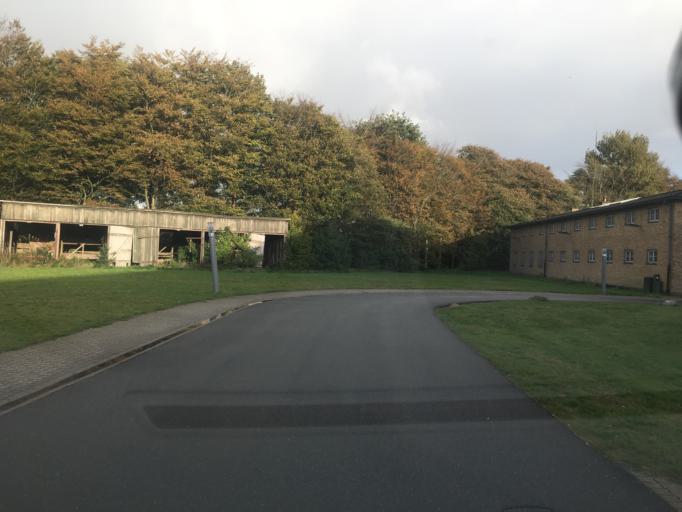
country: DK
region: South Denmark
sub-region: Tonder Kommune
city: Tonder
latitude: 54.9499
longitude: 8.8807
